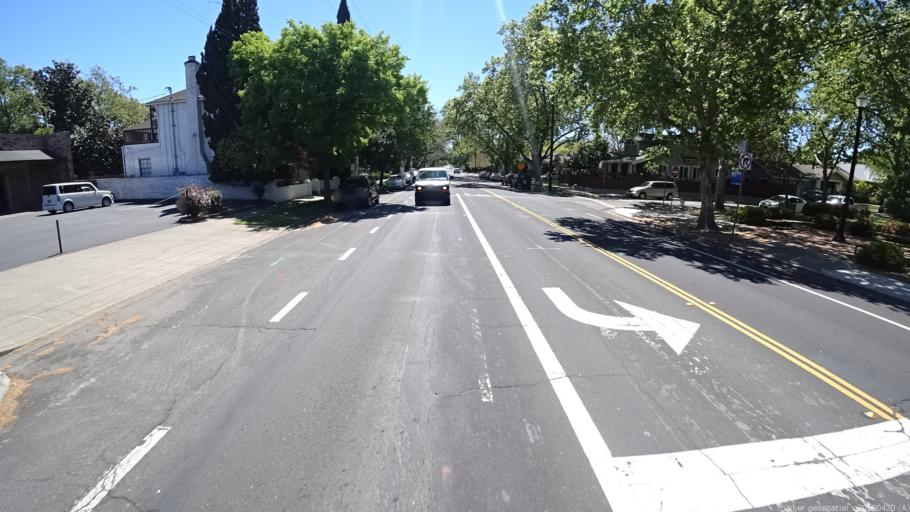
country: US
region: California
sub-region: Sacramento County
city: Sacramento
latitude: 38.5561
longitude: -121.4872
